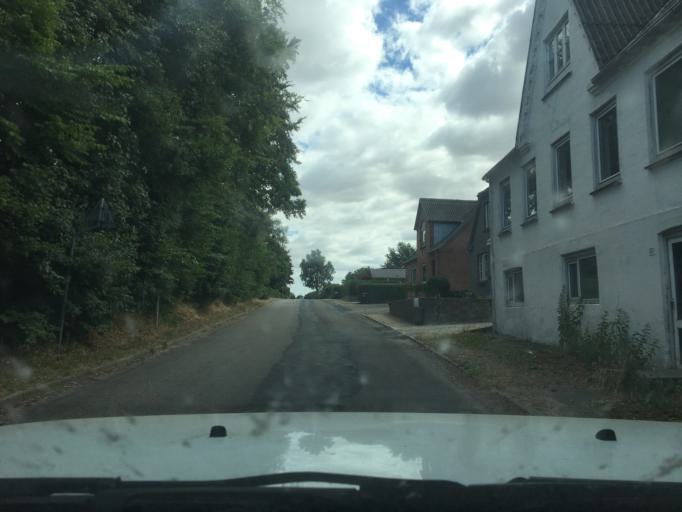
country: DK
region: Central Jutland
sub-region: Syddjurs Kommune
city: Ryomgard
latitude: 56.4613
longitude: 10.6362
